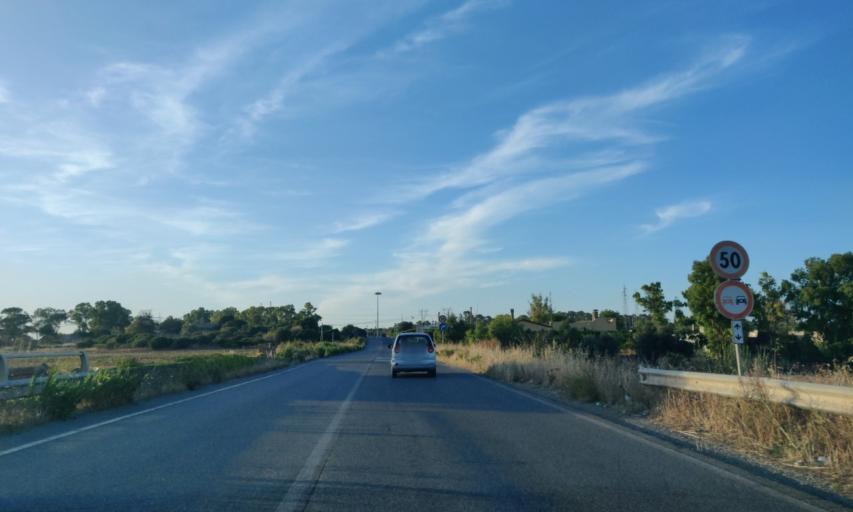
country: IT
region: Latium
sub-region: Citta metropolitana di Roma Capitale
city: Aurelia
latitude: 42.1281
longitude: 11.7731
